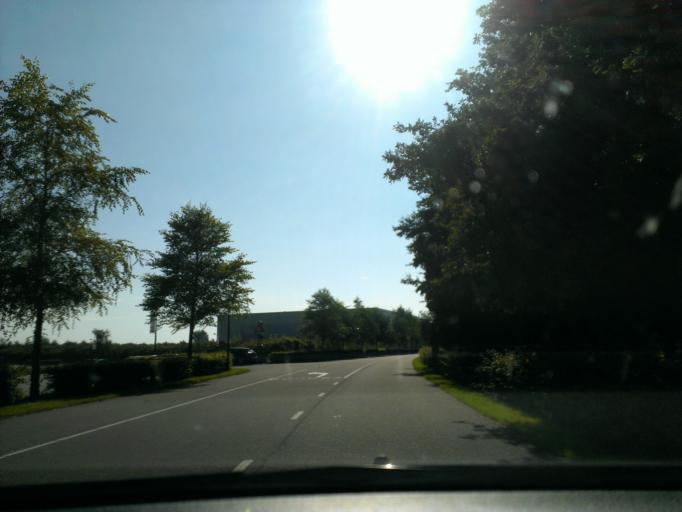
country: NL
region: Drenthe
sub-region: Gemeente Coevorden
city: Dalen
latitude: 52.6796
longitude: 6.7705
